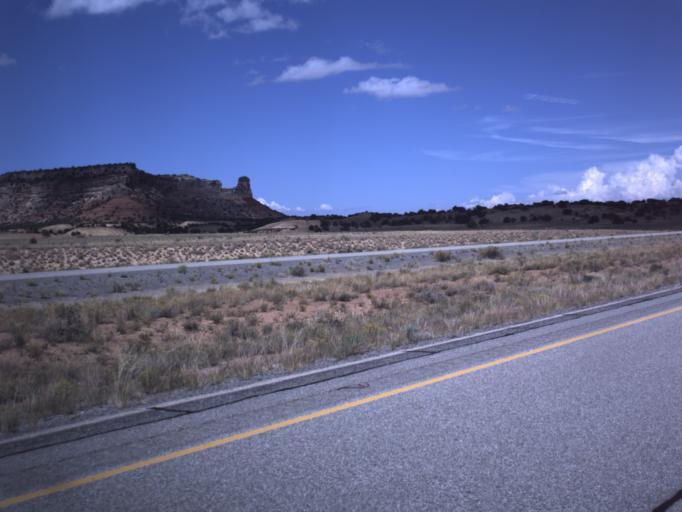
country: US
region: Utah
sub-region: Emery County
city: Castle Dale
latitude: 38.8724
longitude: -110.6833
